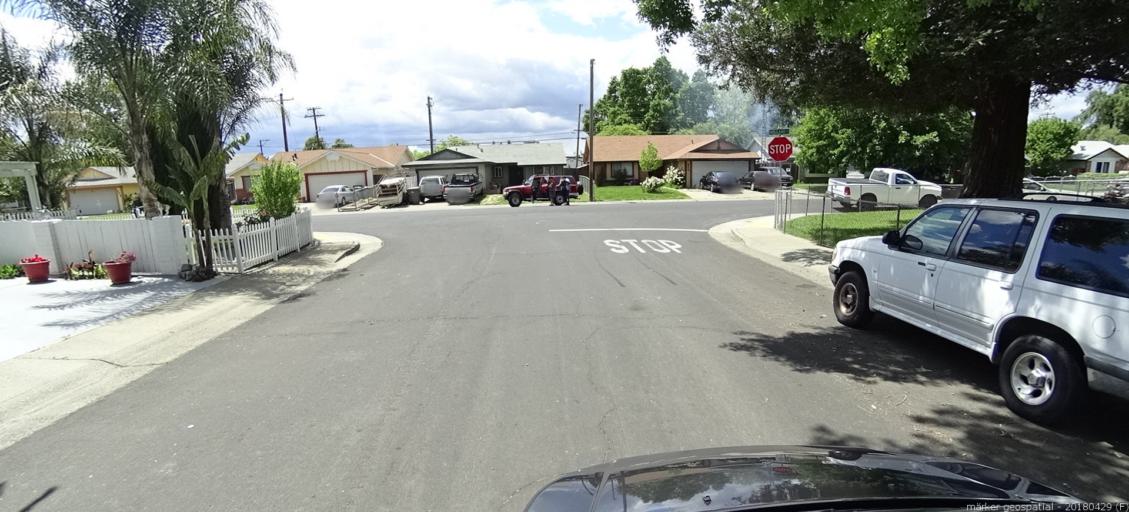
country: US
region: California
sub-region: Yolo County
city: West Sacramento
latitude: 38.5969
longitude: -121.5299
